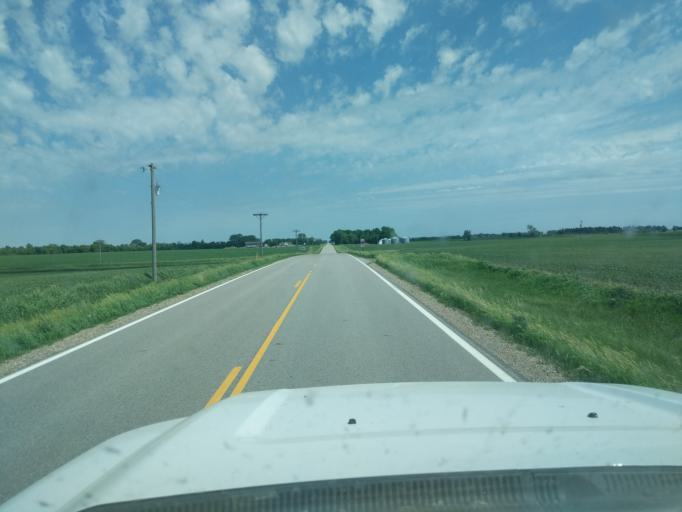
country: US
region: Minnesota
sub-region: Yellow Medicine County
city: Granite Falls
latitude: 44.7582
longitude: -95.4014
